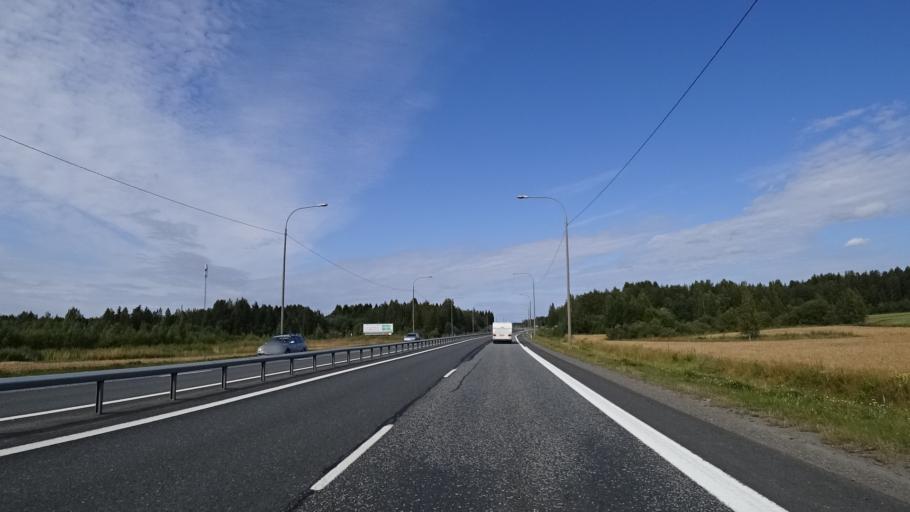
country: FI
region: North Karelia
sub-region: Joensuu
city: Joensuu
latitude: 62.5499
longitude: 29.8414
